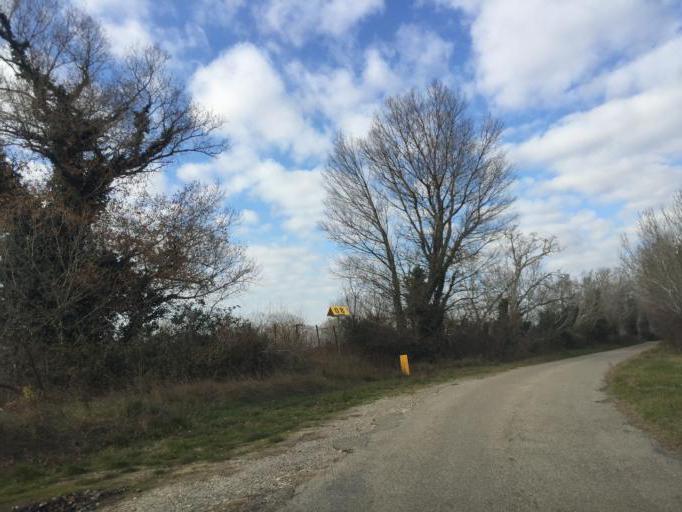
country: FR
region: Provence-Alpes-Cote d'Azur
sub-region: Departement du Vaucluse
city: Jonquieres
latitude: 44.0962
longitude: 4.9221
